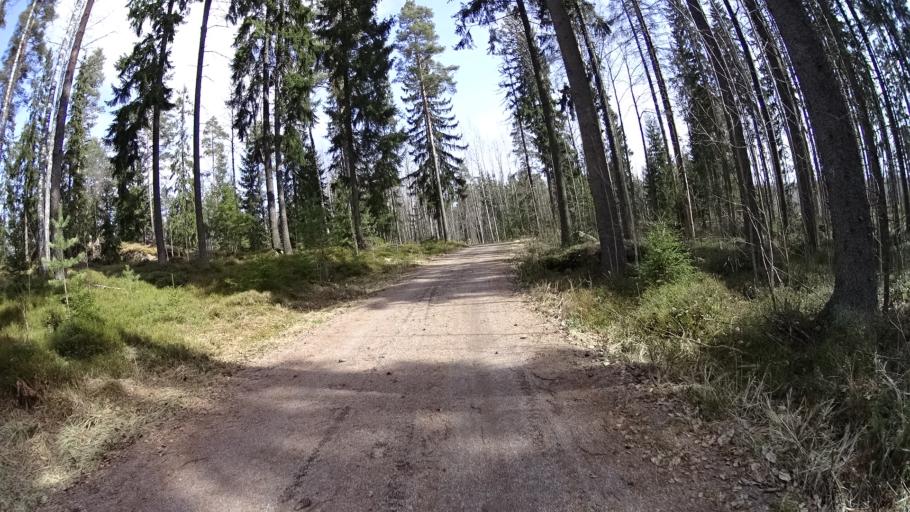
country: FI
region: Uusimaa
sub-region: Helsinki
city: Kilo
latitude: 60.3124
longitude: 24.8086
